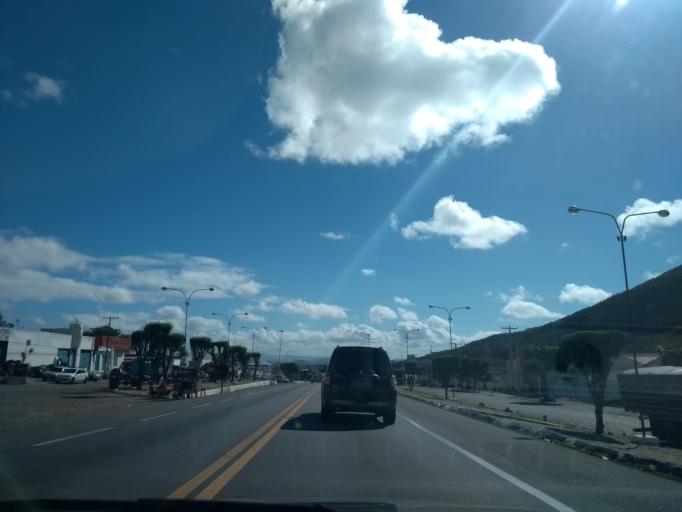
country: BR
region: Bahia
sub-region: Amargosa
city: Amargosa
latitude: -12.8753
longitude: -39.8571
